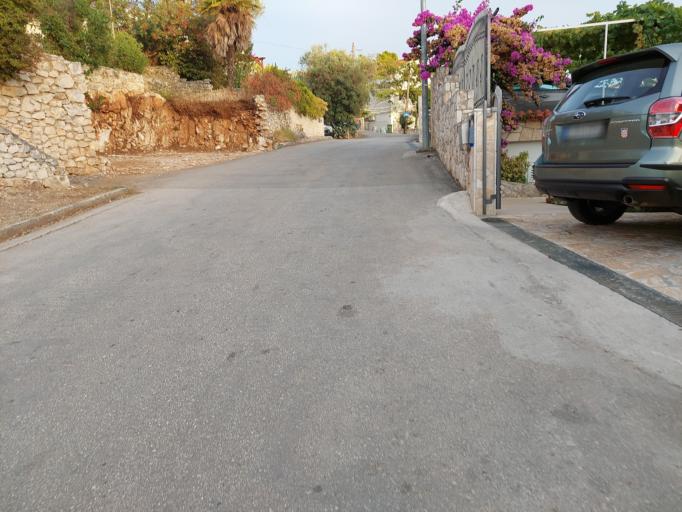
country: HR
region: Splitsko-Dalmatinska
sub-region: Grad Trogir
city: Trogir
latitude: 43.4932
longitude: 16.2736
